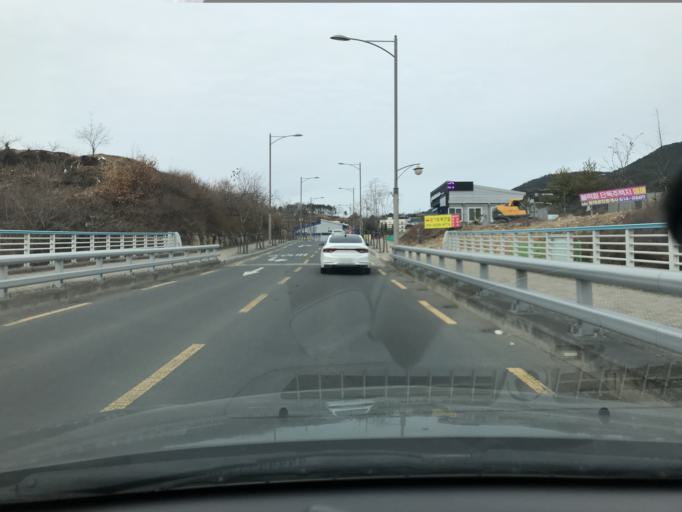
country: KR
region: Daegu
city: Hwawon
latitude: 35.6985
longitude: 128.4540
